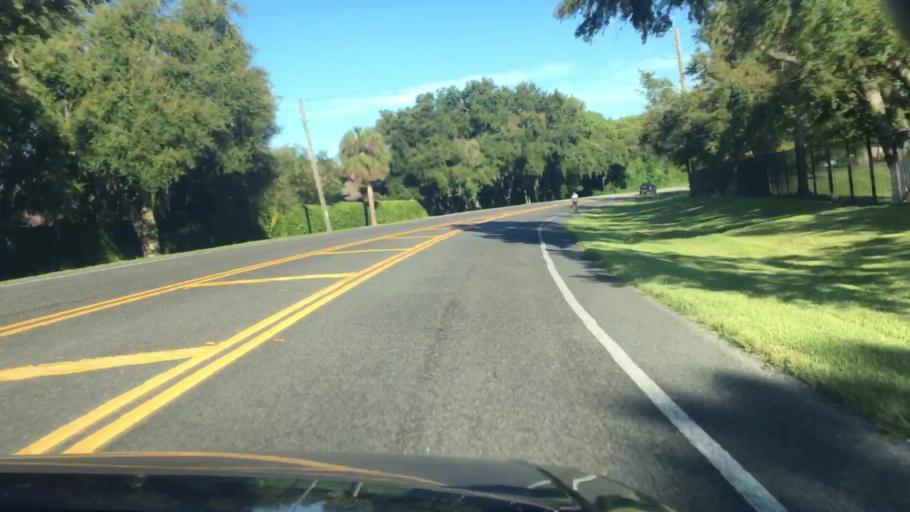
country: US
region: Florida
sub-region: Lake County
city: Eustis
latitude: 28.8513
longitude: -81.6424
